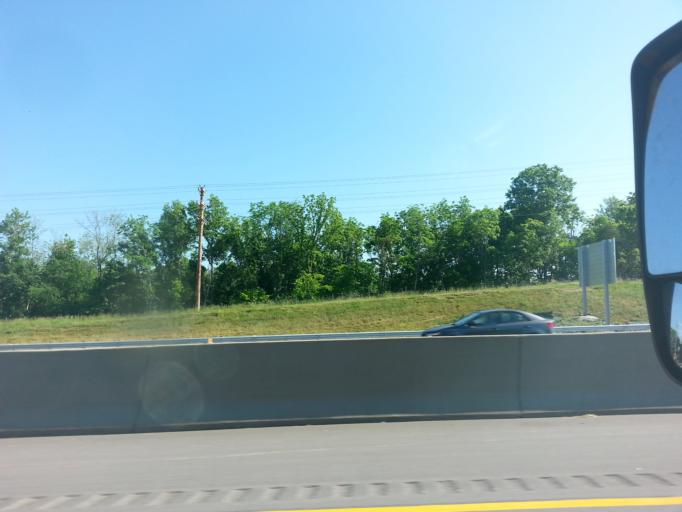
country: US
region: Kentucky
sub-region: Shelby County
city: Simpsonville
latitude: 38.2056
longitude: -85.3350
